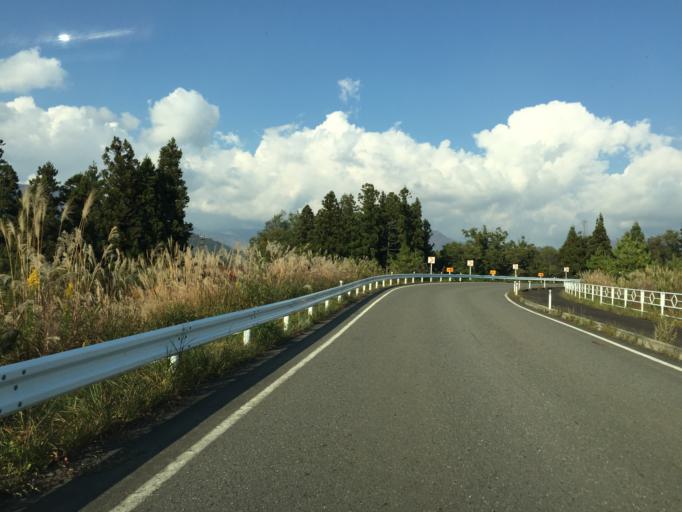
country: JP
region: Fukushima
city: Kitakata
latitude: 37.7210
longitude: 139.8688
